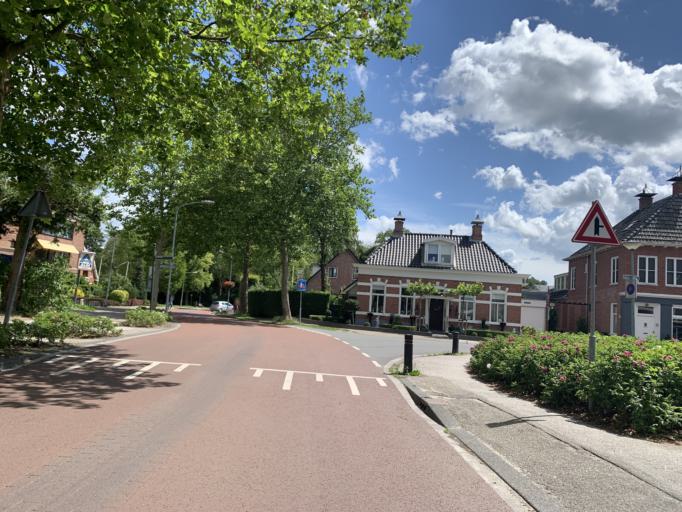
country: NL
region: Groningen
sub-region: Gemeente Haren
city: Haren
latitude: 53.1738
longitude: 6.6090
